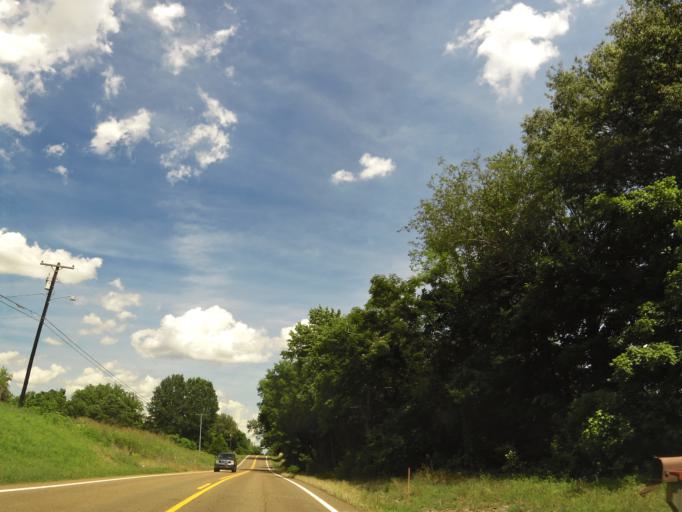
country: US
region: Tennessee
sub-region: Dyer County
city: Dyersburg
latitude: 36.0256
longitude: -89.3101
